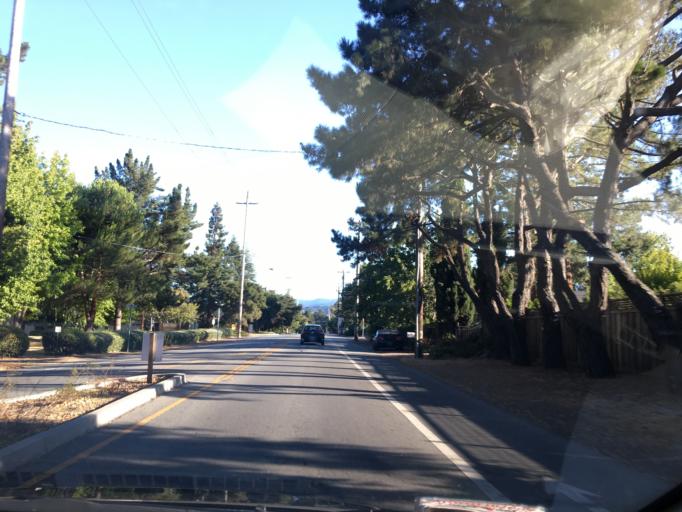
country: US
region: California
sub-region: Santa Clara County
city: Loyola
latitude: 37.3517
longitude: -122.0779
